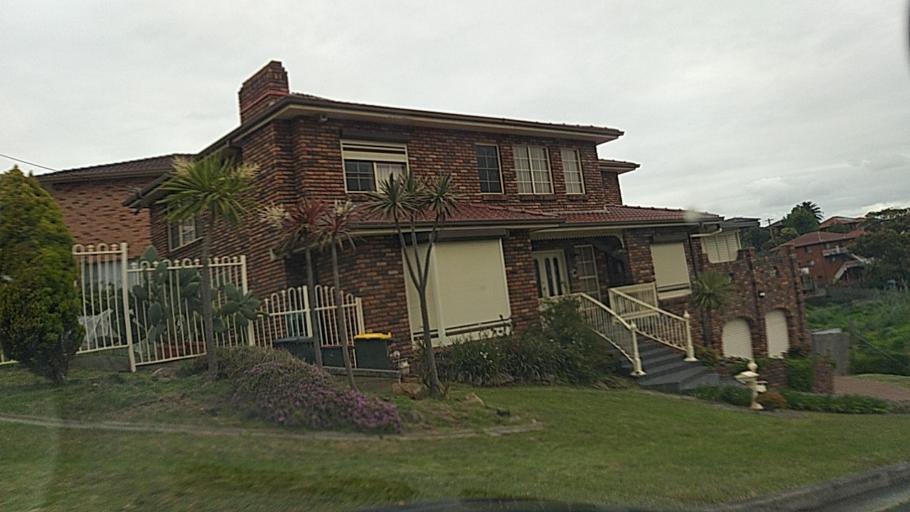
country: AU
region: New South Wales
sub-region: Wollongong
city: Lake Heights
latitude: -34.4860
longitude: 150.8793
